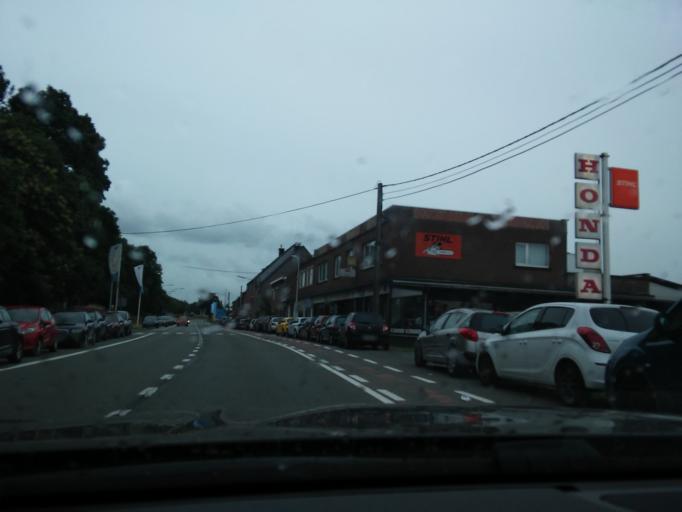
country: BE
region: Wallonia
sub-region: Province du Hainaut
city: Enghien
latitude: 50.6851
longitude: 4.0312
